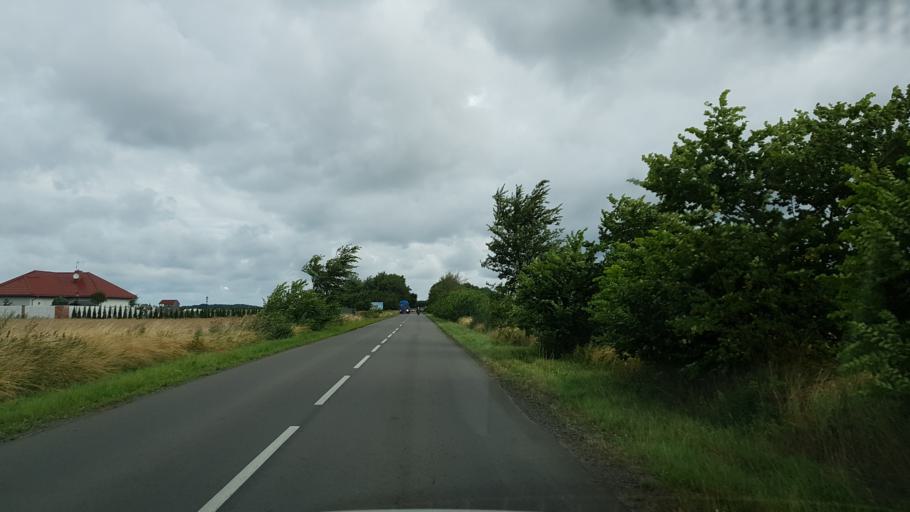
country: PL
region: West Pomeranian Voivodeship
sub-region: Powiat gryficki
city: Rewal
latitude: 54.0620
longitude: 15.0257
